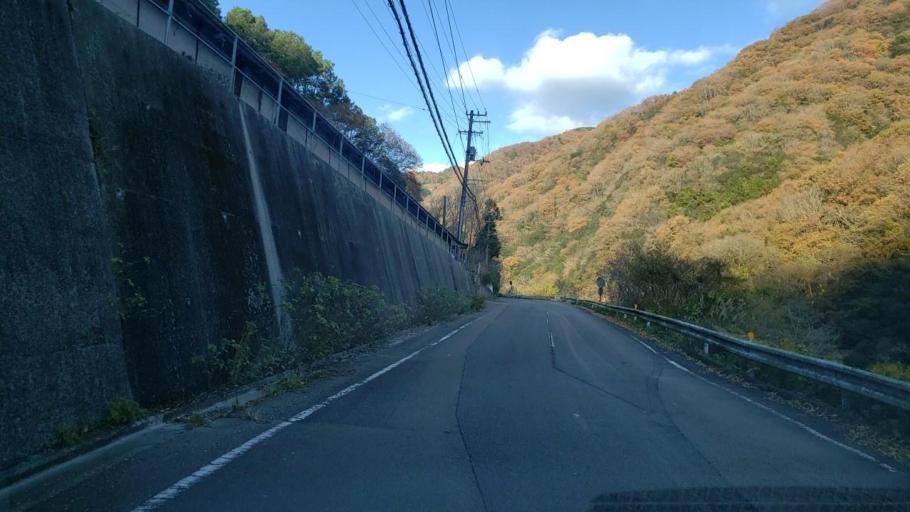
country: JP
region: Tokushima
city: Wakimachi
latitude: 34.0841
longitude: 134.0727
